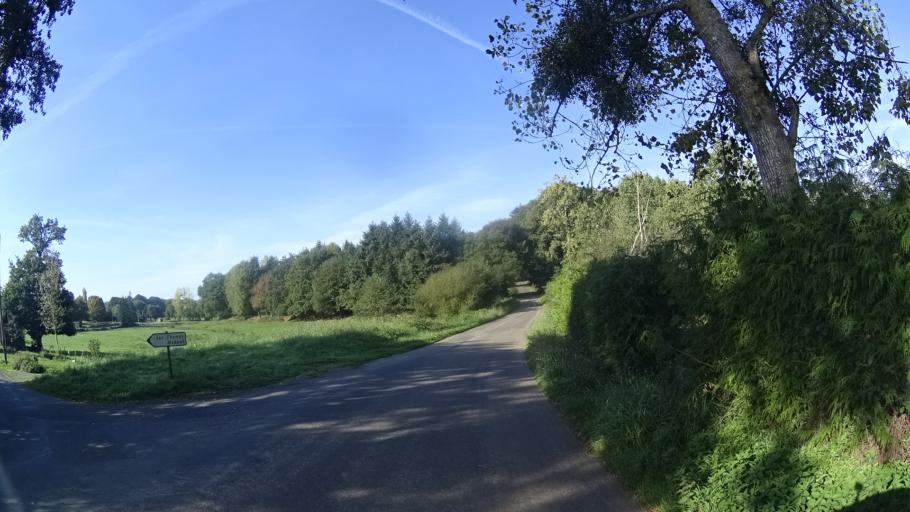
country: FR
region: Brittany
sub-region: Departement du Morbihan
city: Peillac
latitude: 47.7399
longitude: -2.2200
